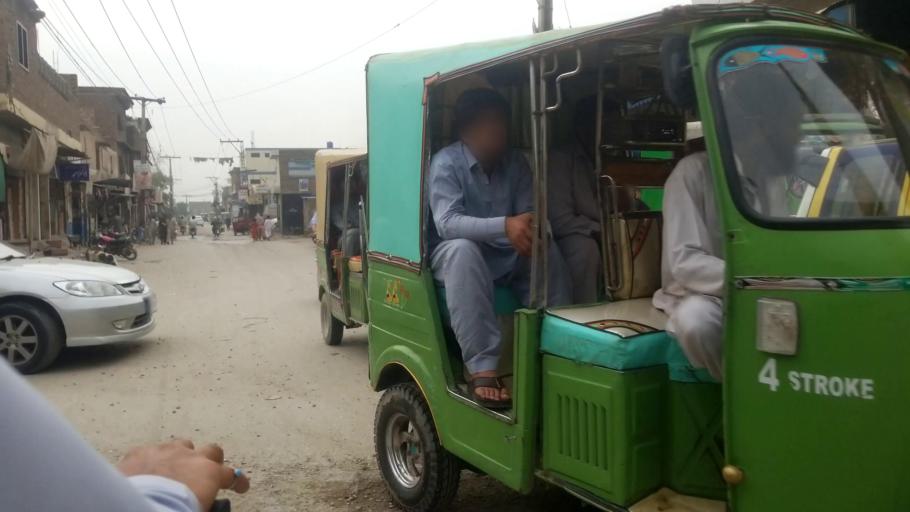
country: PK
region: Khyber Pakhtunkhwa
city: Peshawar
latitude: 33.9895
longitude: 71.5492
